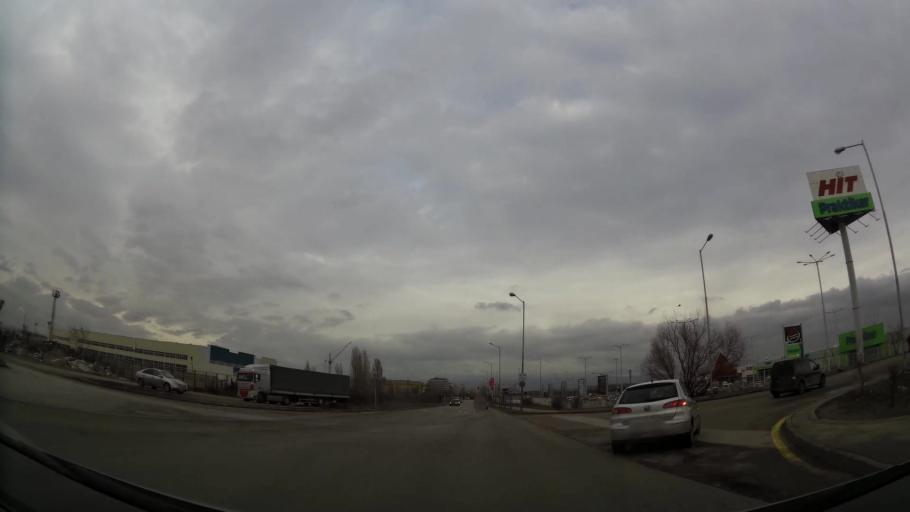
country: BG
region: Sofia-Capital
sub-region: Stolichna Obshtina
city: Sofia
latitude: 42.7297
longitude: 23.2650
